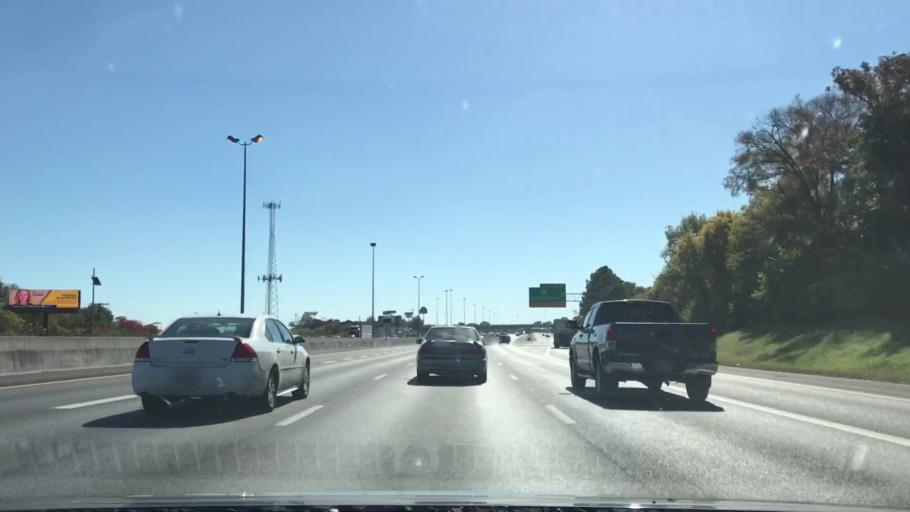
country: US
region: Tennessee
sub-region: Davidson County
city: Oak Hill
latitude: 36.0908
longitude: -86.7634
